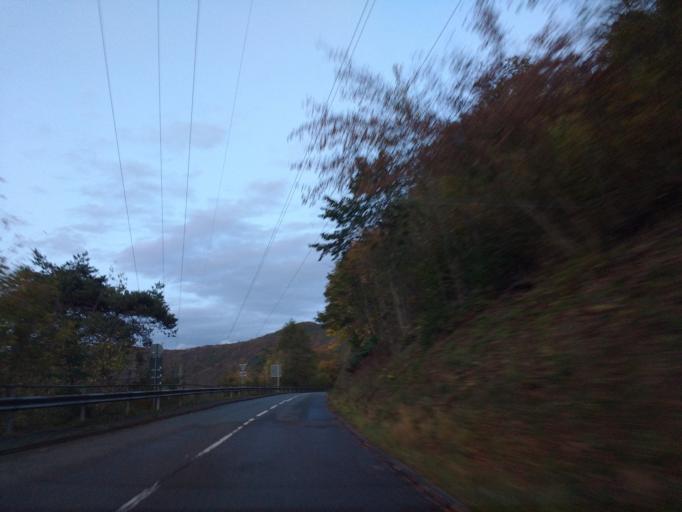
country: DE
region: Hesse
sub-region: Regierungsbezirk Kassel
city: Waldeck
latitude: 51.1702
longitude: 9.0558
